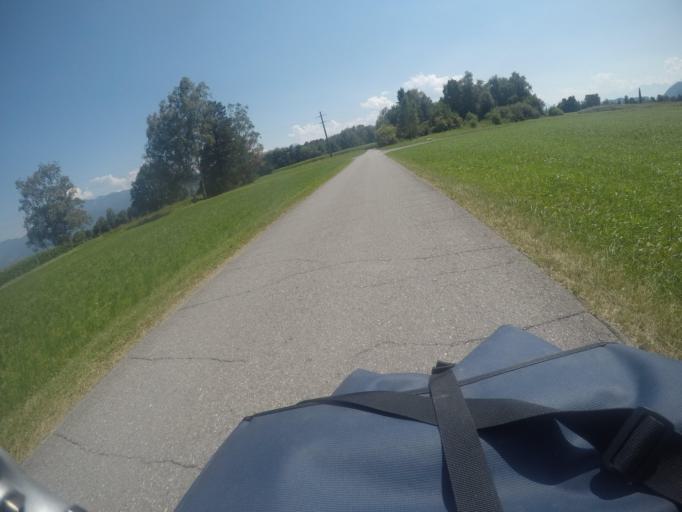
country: AT
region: Vorarlberg
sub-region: Politischer Bezirk Feldkirch
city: Koblach
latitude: 47.3514
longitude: 9.5778
